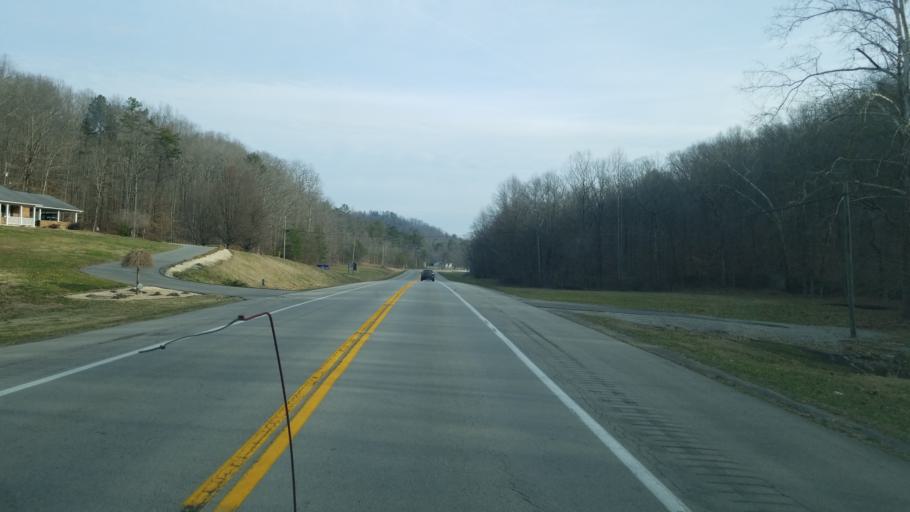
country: US
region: Kentucky
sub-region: Russell County
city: Russell Springs
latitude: 37.1572
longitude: -85.0219
